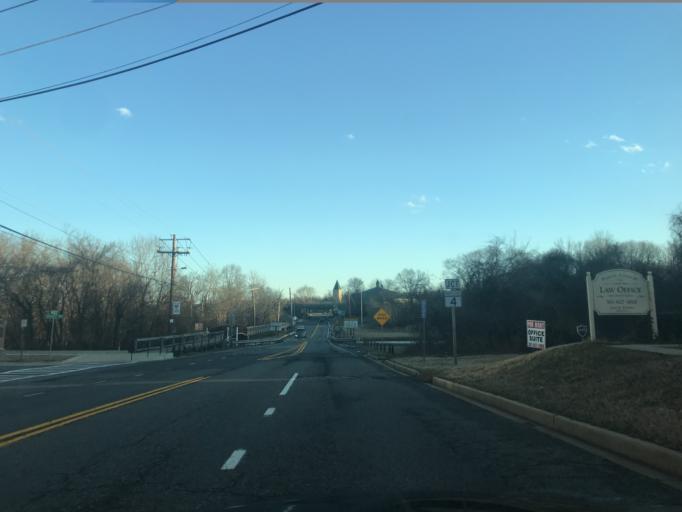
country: US
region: Maryland
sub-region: Prince George's County
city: Upper Marlboro
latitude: 38.8151
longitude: -76.7512
